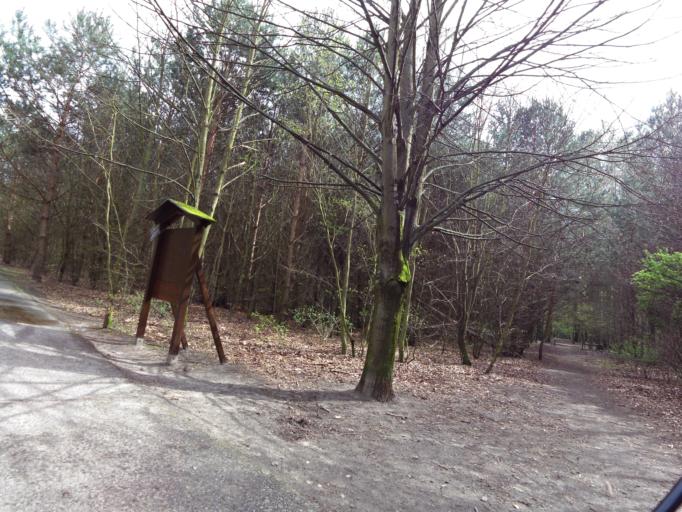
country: DE
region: Berlin
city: Lichtenrade
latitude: 52.3761
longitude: 13.4106
